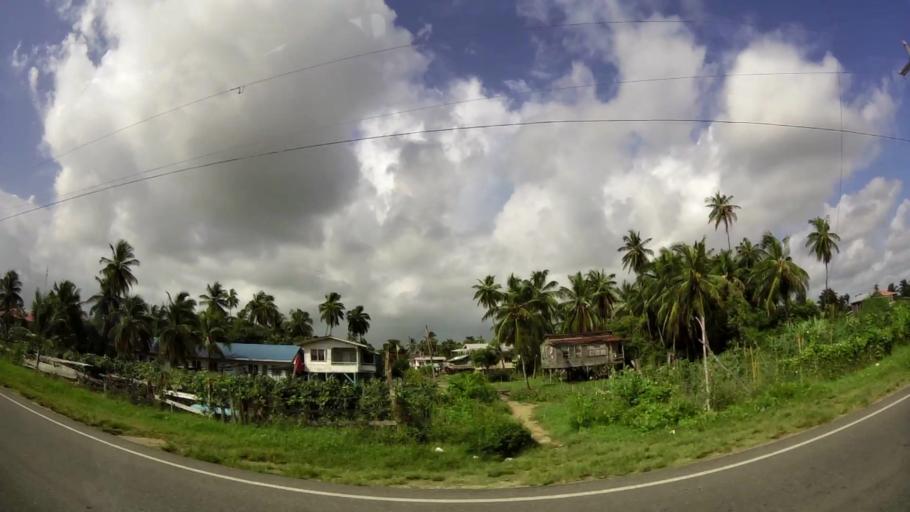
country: GY
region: Demerara-Mahaica
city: Mahaica Village
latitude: 6.6770
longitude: -57.9215
